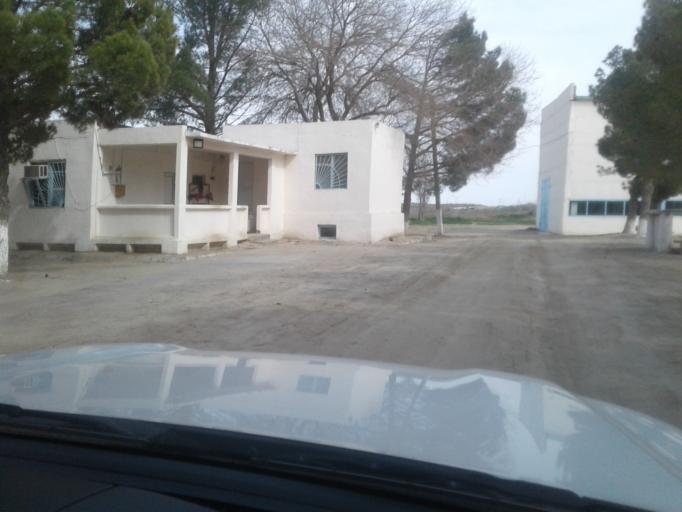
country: TM
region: Ahal
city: Ashgabat
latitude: 38.1349
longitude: 58.3672
